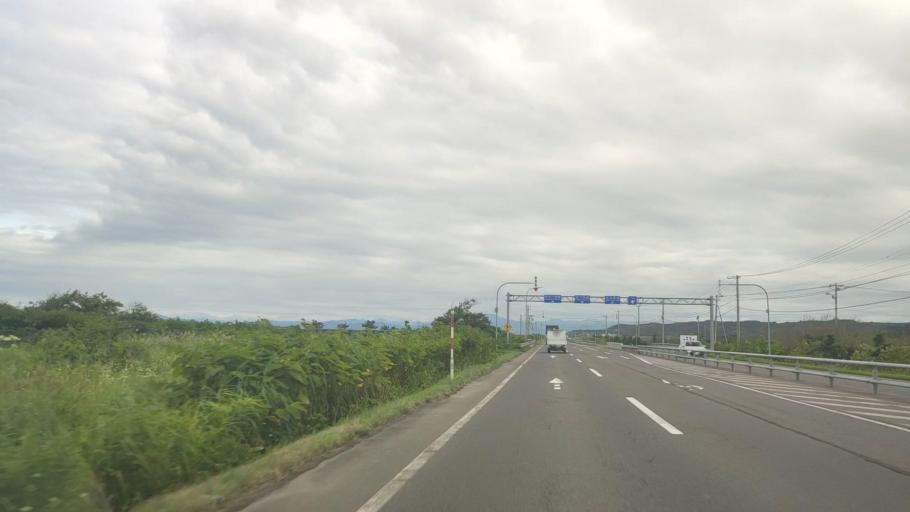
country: JP
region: Hokkaido
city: Niseko Town
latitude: 42.4049
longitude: 140.3049
